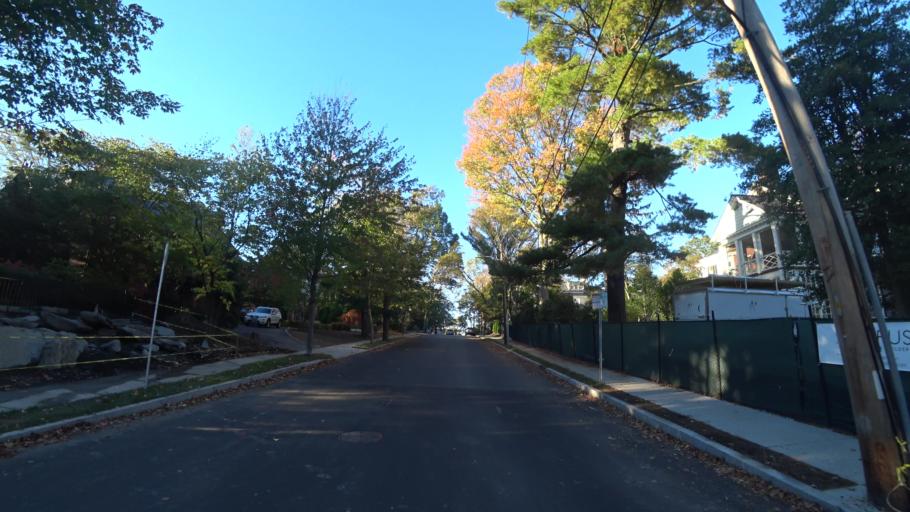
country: US
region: Massachusetts
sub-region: Middlesex County
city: Cambridge
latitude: 42.3791
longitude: -71.1338
